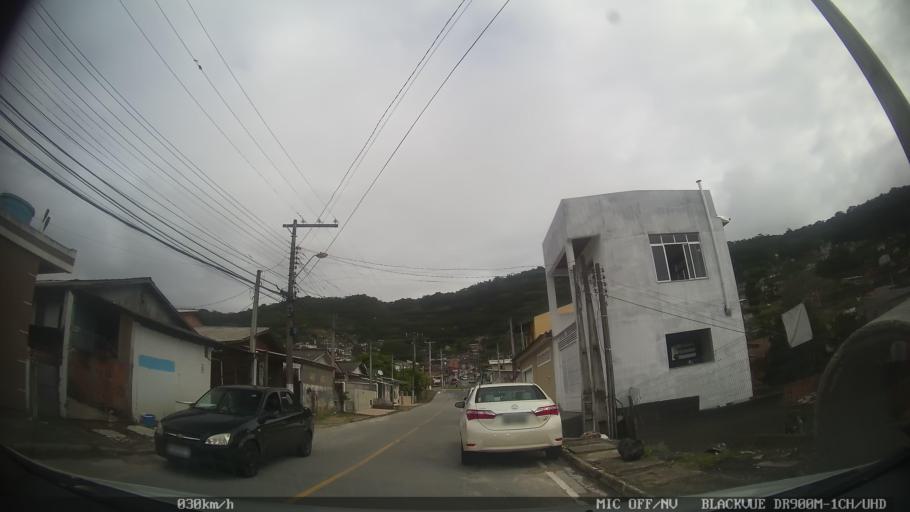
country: BR
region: Santa Catarina
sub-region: Biguacu
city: Biguacu
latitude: -27.5432
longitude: -48.6482
